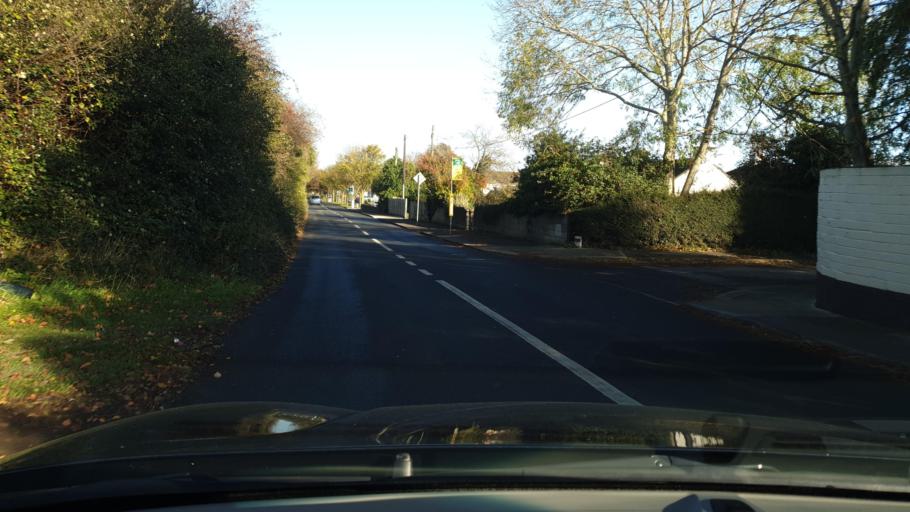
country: IE
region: Leinster
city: Lucan
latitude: 53.3448
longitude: -6.4448
